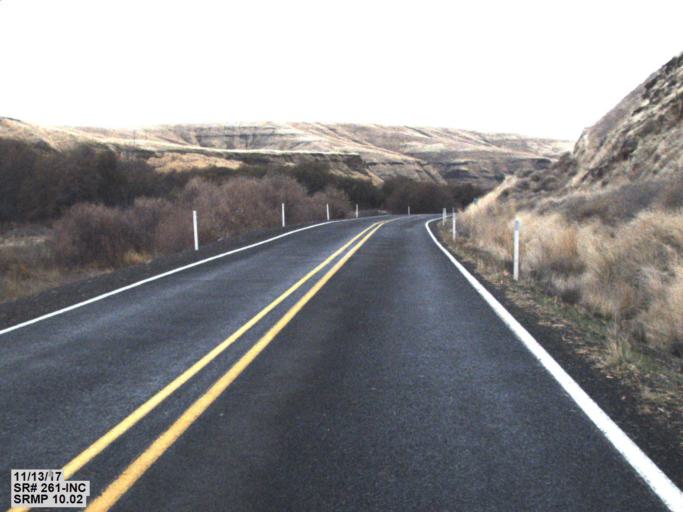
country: US
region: Washington
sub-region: Walla Walla County
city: Waitsburg
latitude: 46.5402
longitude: -118.1565
